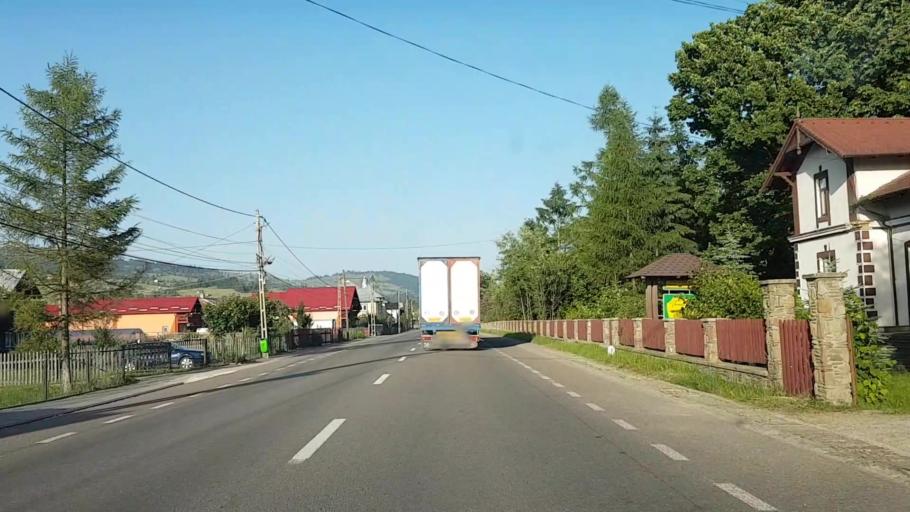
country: RO
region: Suceava
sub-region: Comuna Dorna Candrenilor
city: Dorna Candrenilor
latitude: 47.3558
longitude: 25.2462
